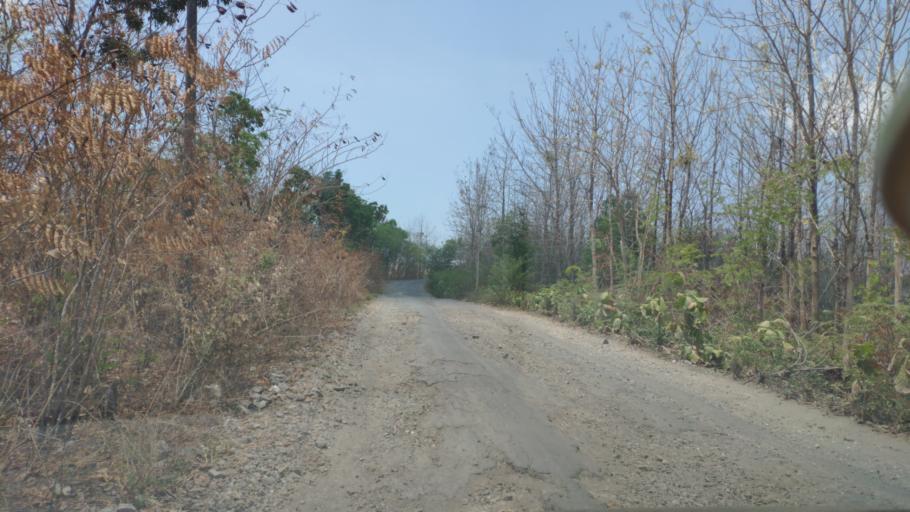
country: ID
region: Central Java
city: Randublatung
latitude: -7.2346
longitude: 111.3810
